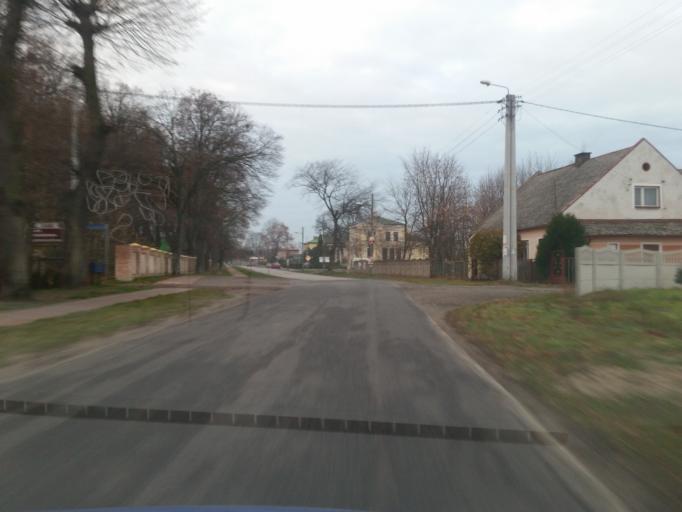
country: PL
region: Silesian Voivodeship
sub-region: Powiat czestochowski
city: Borowno
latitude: 50.9669
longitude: 19.2828
